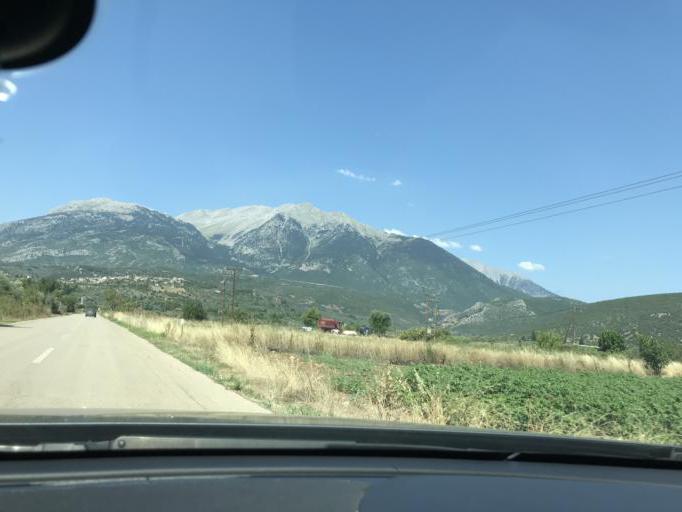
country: GR
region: Central Greece
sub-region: Nomos Fthiotidos
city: Kato Tithorea
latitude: 38.5191
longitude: 22.7620
